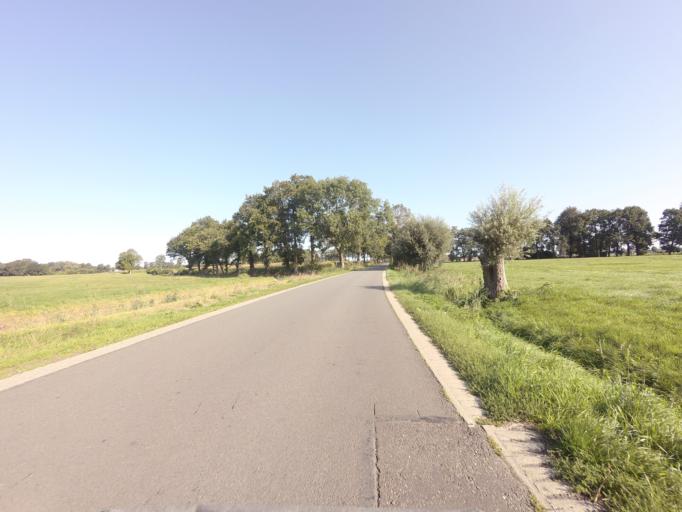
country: NL
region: Overijssel
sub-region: Gemeente Raalte
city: Raalte
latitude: 52.4008
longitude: 6.2838
